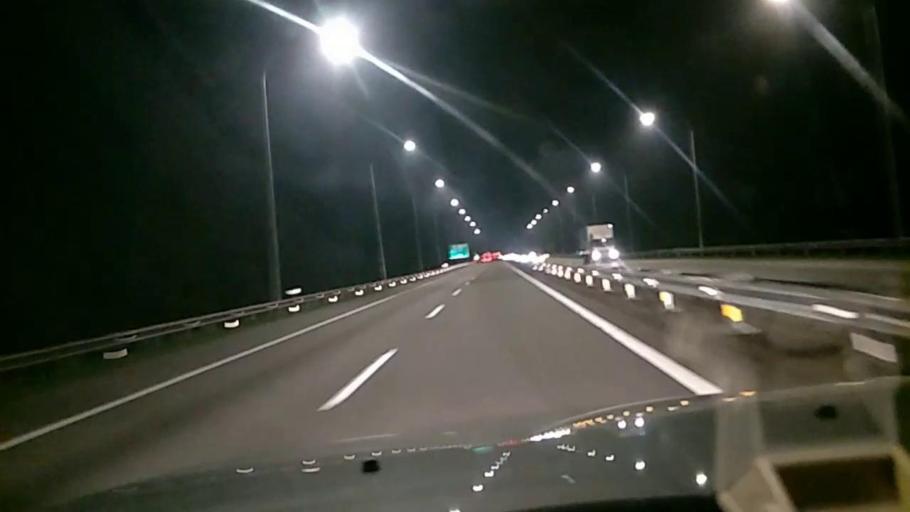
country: MY
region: Perak
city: Bagan Serai
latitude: 5.0715
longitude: 100.5880
